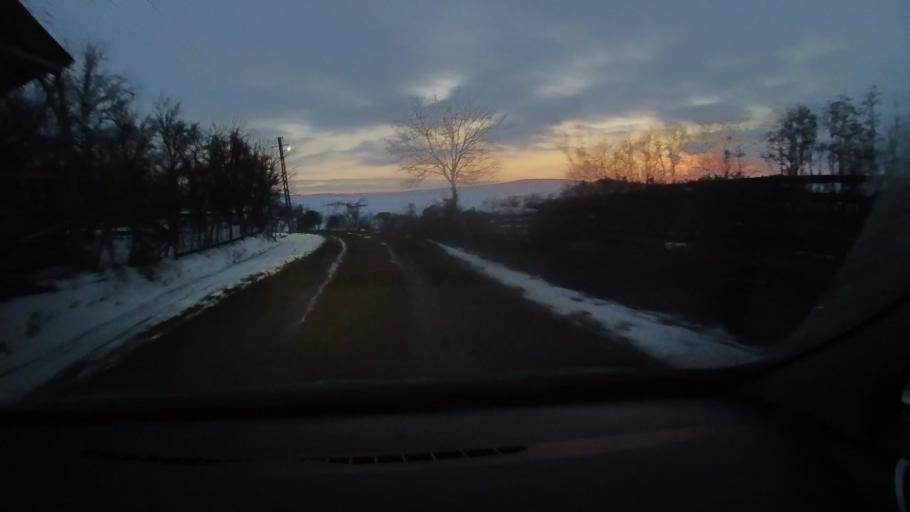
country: RO
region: Harghita
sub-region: Comuna Darjiu
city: Darjiu
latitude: 46.1696
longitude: 25.2276
